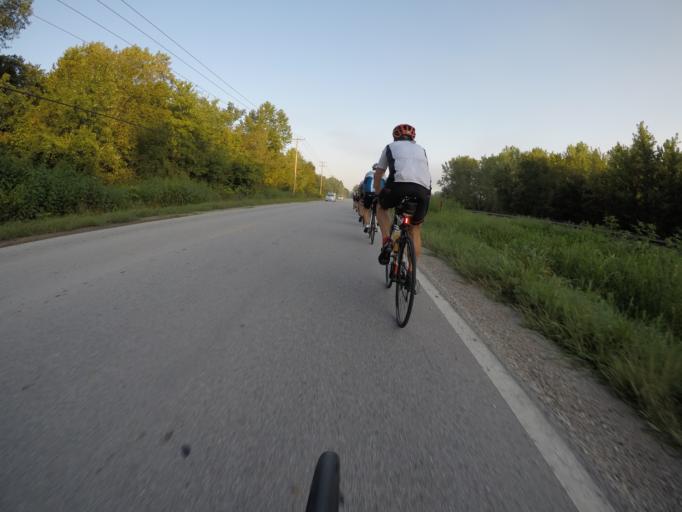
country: US
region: Kansas
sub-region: Leavenworth County
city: Lansing
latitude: 39.1896
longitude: -94.8027
